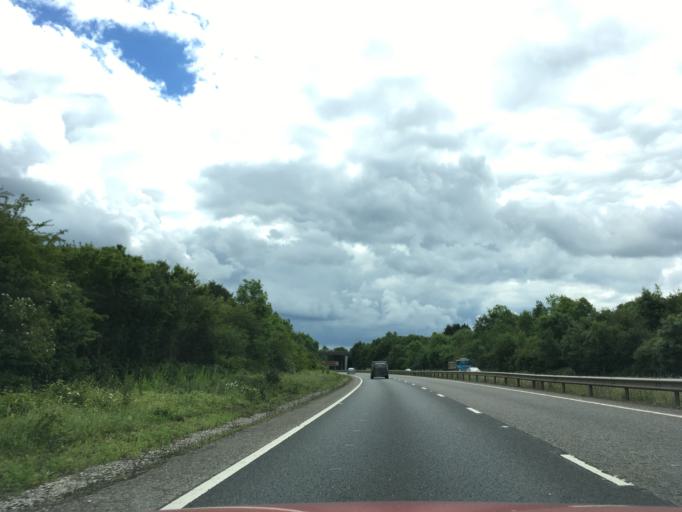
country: GB
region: England
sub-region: Milton Keynes
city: Milton Keynes
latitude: 52.0148
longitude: -0.7542
